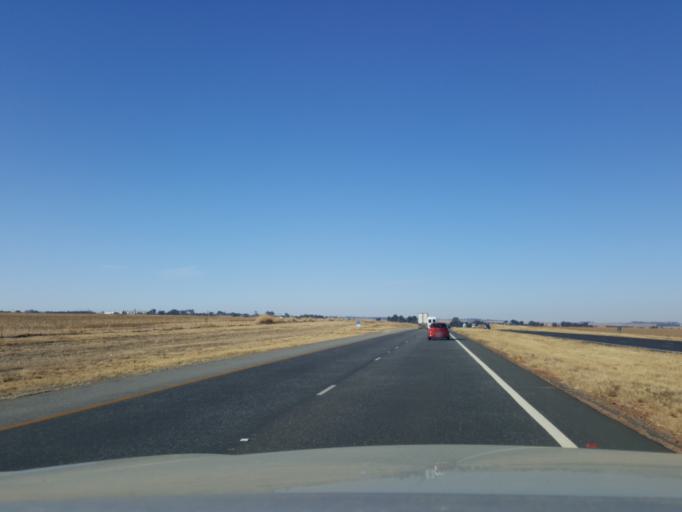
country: ZA
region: Mpumalanga
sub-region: Nkangala District Municipality
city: Belfast
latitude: -25.8204
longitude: 29.8677
